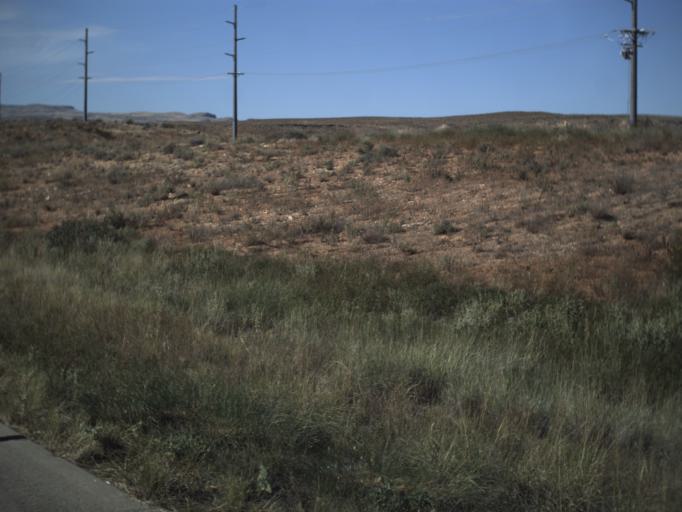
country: US
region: Utah
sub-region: Washington County
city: Saint George
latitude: 37.0151
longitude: -113.6148
